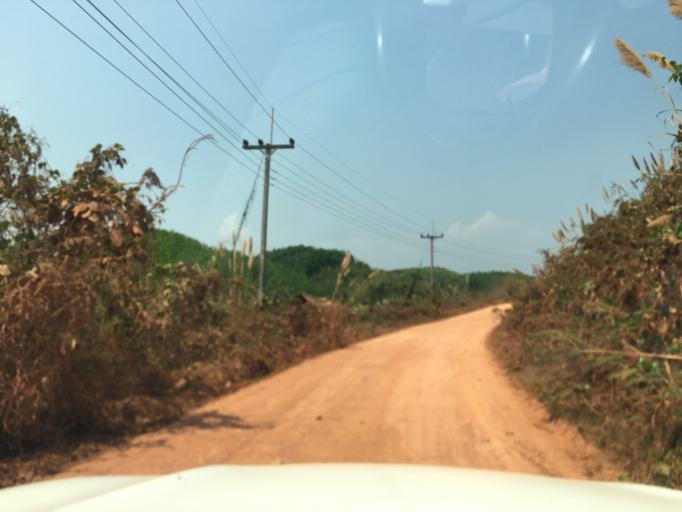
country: LA
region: Bolikhamxai
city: Bolikhan
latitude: 18.7301
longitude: 103.6325
